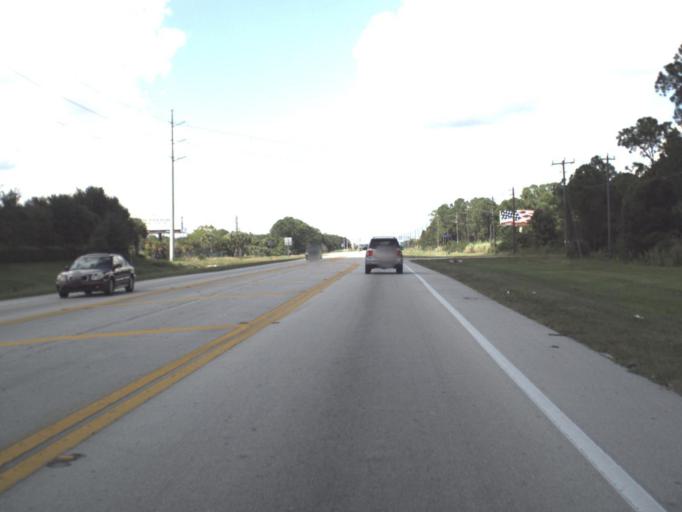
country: US
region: Florida
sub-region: Lee County
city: Gateway
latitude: 26.6097
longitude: -81.7575
